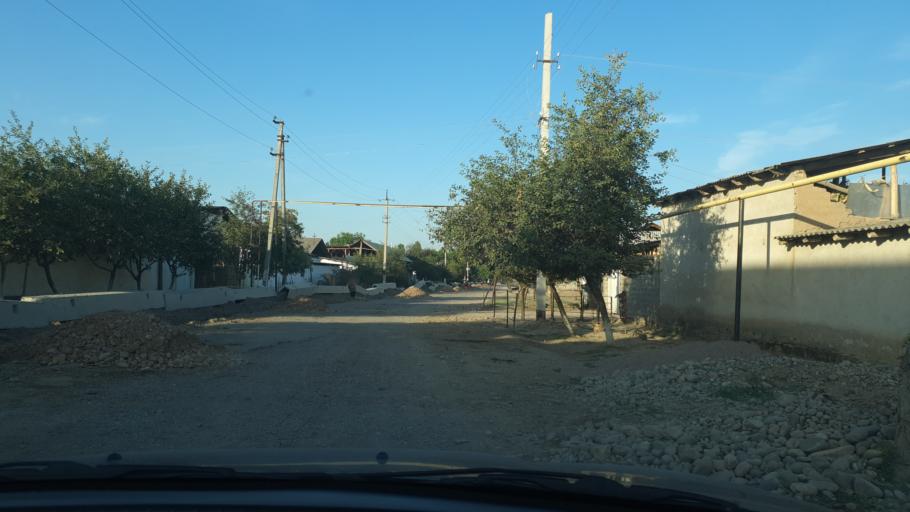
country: UZ
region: Toshkent
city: Tuytepa
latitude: 41.1046
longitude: 69.3899
